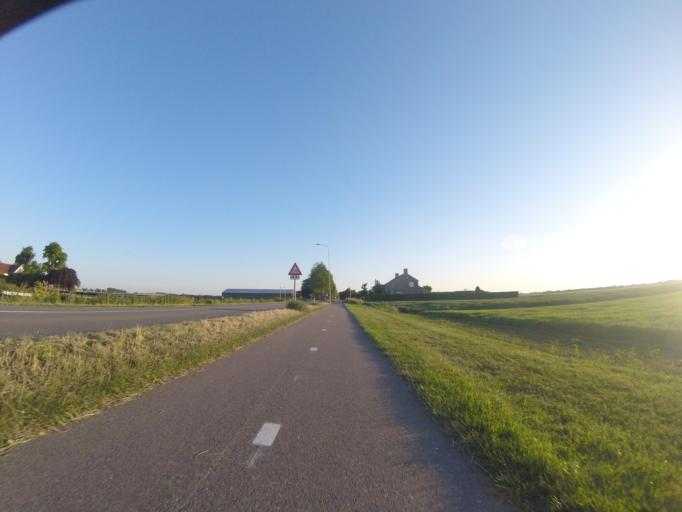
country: NL
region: North Holland
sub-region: Gemeente Haarlemmermeer
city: Hoofddorp
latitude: 52.3695
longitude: 4.7444
